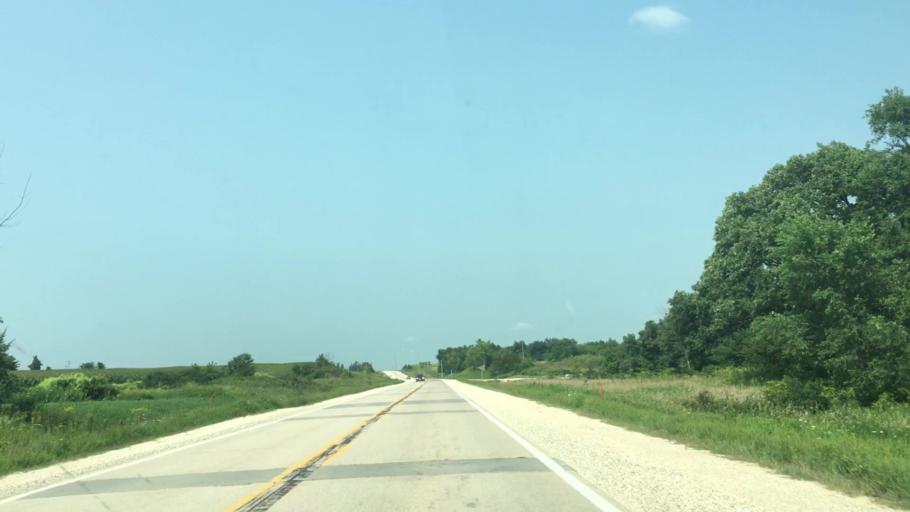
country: US
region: Iowa
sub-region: Fayette County
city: West Union
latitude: 43.1249
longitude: -91.8695
